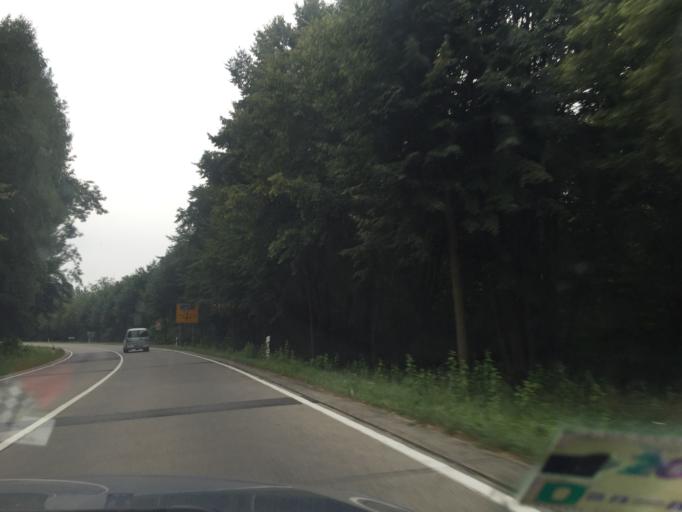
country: DE
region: Brandenburg
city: Wandlitz
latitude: 52.7481
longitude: 13.4291
